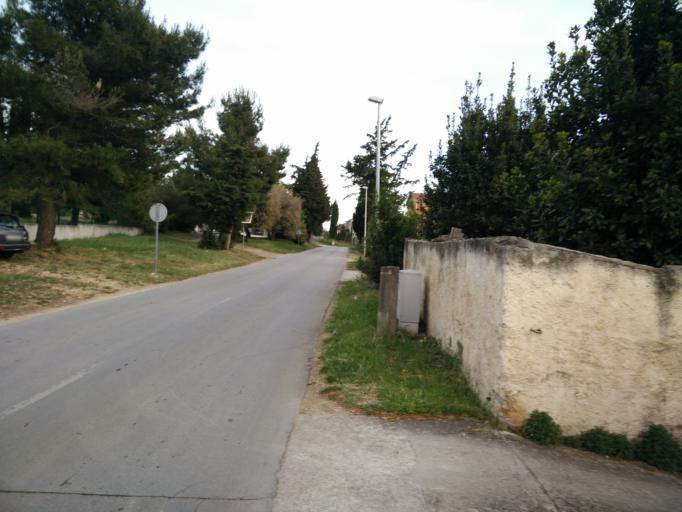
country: HR
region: Zadarska
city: Biograd na Moru
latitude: 43.9484
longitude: 15.4451
